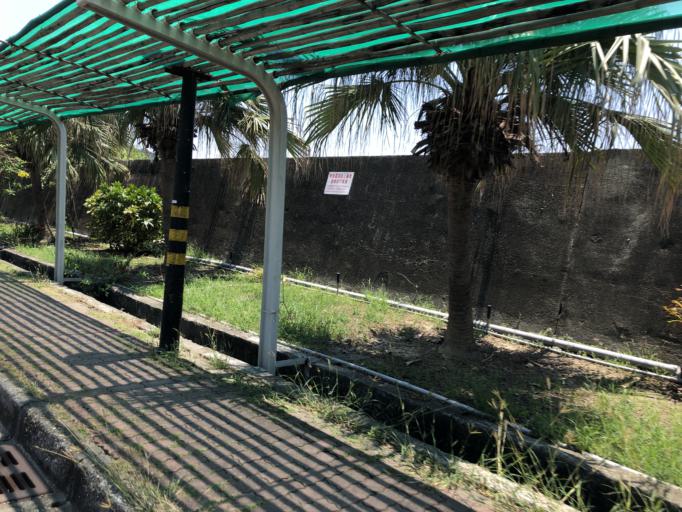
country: TW
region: Kaohsiung
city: Kaohsiung
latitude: 22.6284
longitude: 120.2628
